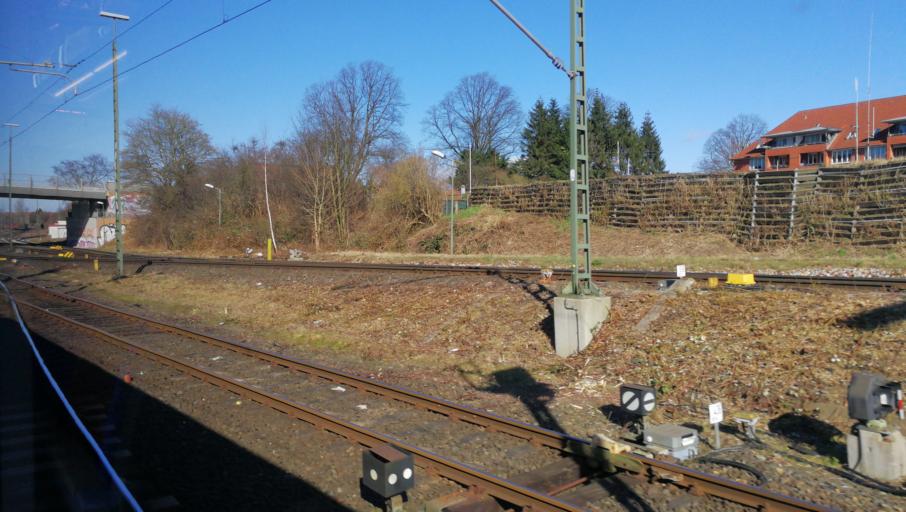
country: DE
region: Schleswig-Holstein
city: Luebeck
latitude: 53.8492
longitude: 10.6560
